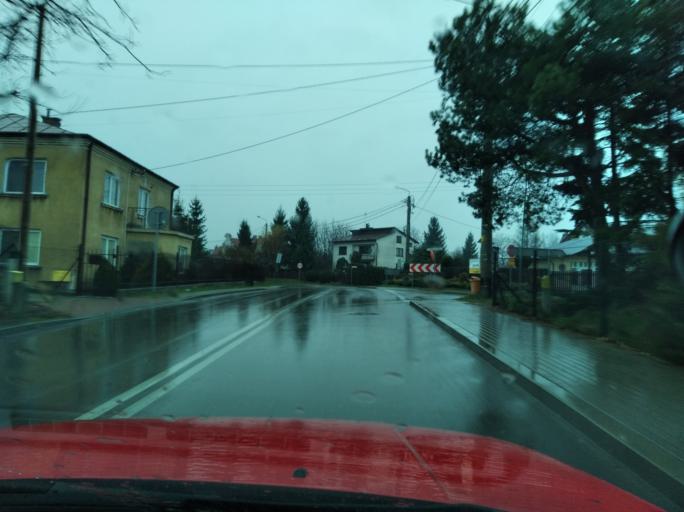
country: PL
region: Subcarpathian Voivodeship
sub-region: Powiat lancucki
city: Lancut
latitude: 50.0704
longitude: 22.2201
